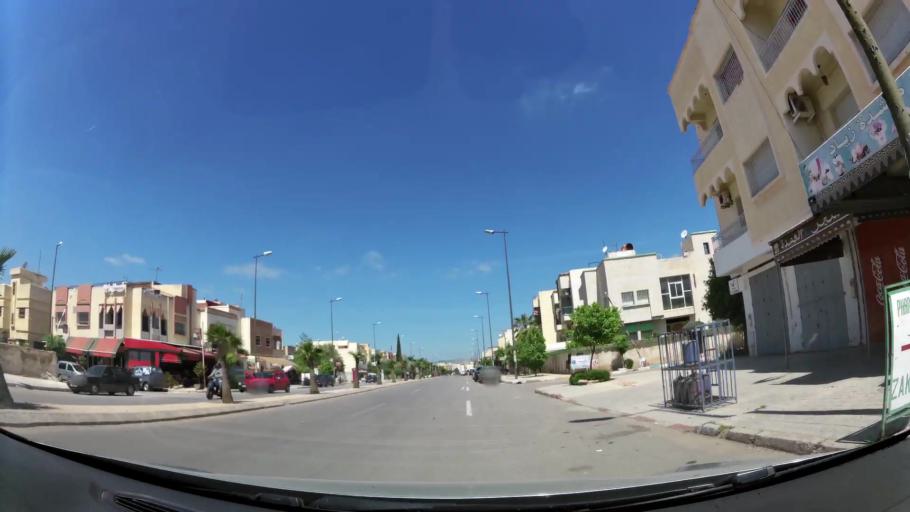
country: MA
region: Fes-Boulemane
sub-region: Fes
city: Fes
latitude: 34.0248
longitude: -5.0181
